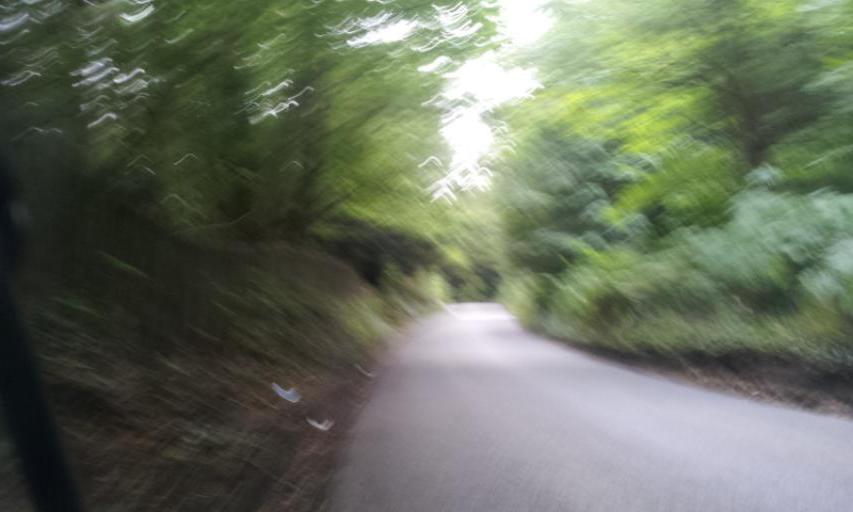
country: GB
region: England
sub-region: Kent
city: Hadlow
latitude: 51.2322
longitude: 0.2959
